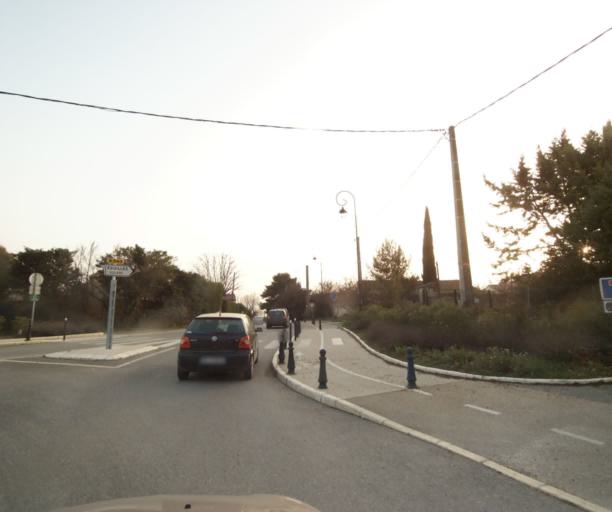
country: FR
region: Provence-Alpes-Cote d'Azur
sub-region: Departement des Bouches-du-Rhone
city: Eguilles
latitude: 43.5733
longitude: 5.3618
